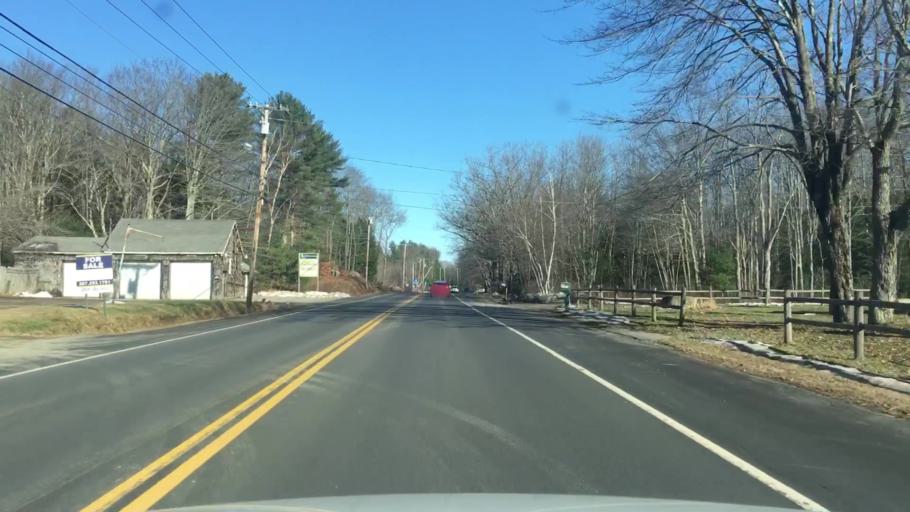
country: US
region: Maine
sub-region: York County
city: Arundel
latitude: 43.4307
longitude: -70.5088
